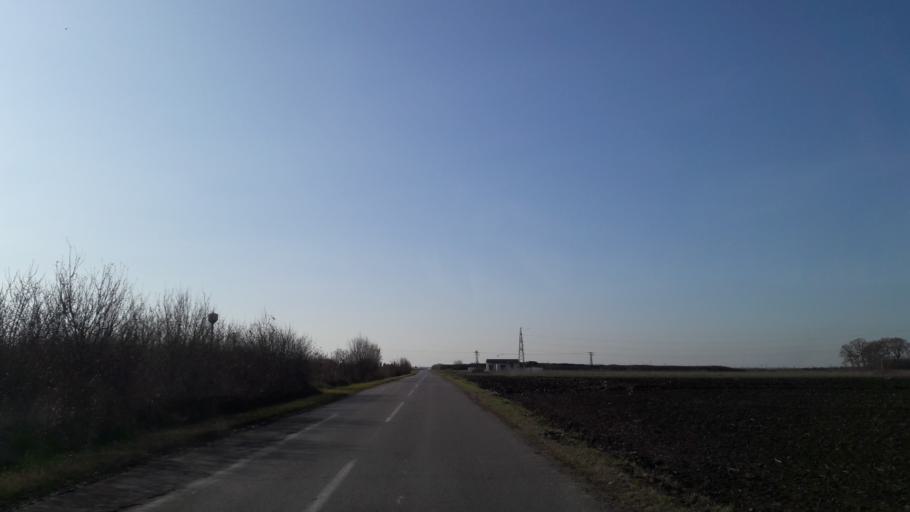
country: HR
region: Osjecko-Baranjska
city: Tenja
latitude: 45.4871
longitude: 18.7256
